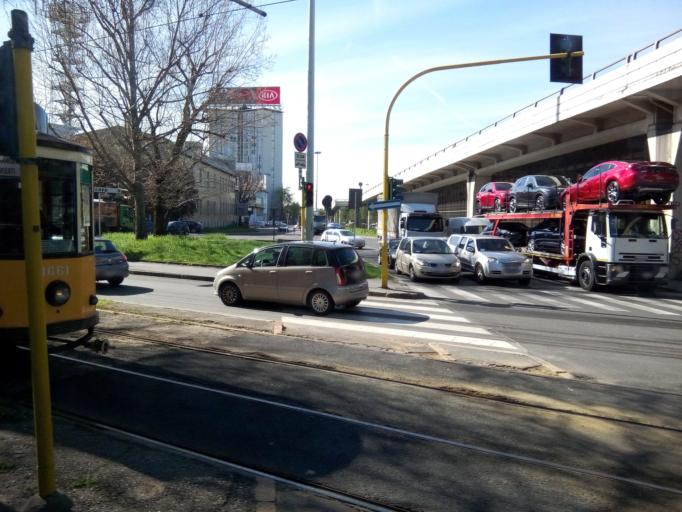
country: IT
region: Lombardy
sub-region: Citta metropolitana di Milano
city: Baranzate
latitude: 45.4995
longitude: 9.1303
